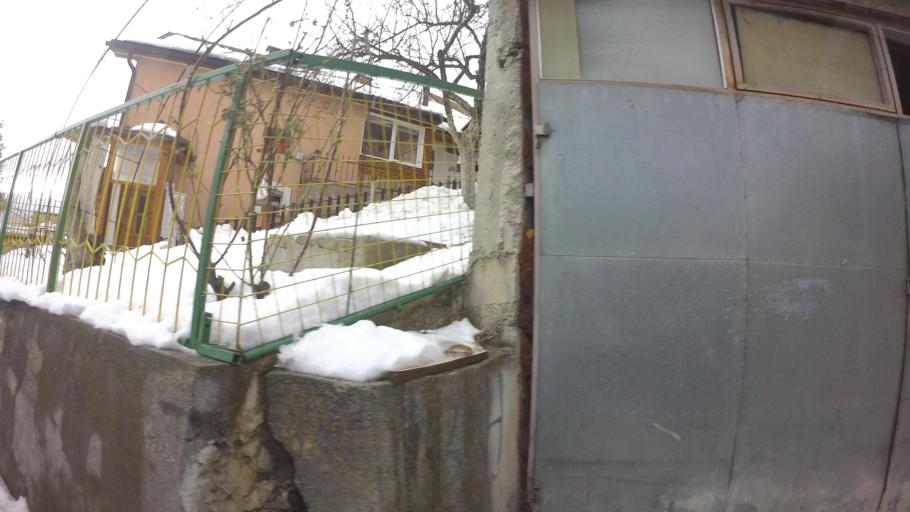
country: BA
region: Federation of Bosnia and Herzegovina
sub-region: Kanton Sarajevo
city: Sarajevo
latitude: 43.8615
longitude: 18.3431
